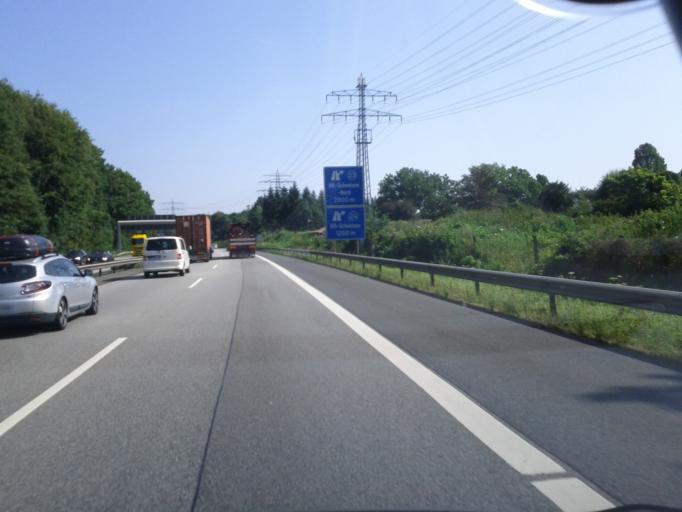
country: DE
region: Hamburg
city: Eidelstedt
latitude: 53.6235
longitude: 9.9179
